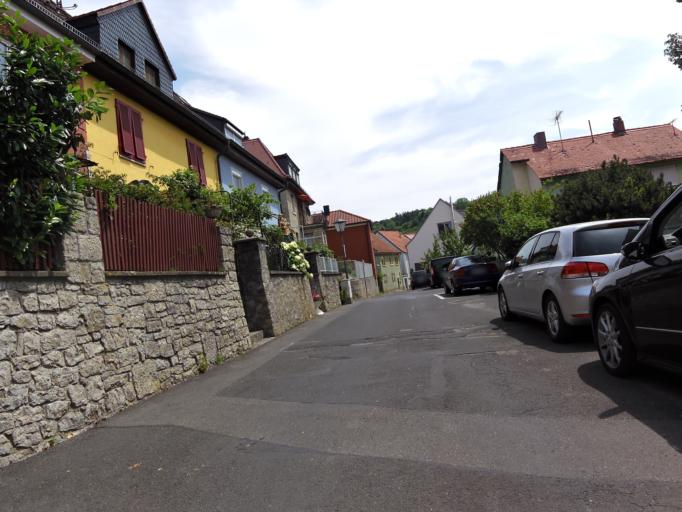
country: DE
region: Bavaria
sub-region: Regierungsbezirk Unterfranken
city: Randersacker
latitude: 49.7608
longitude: 9.9785
